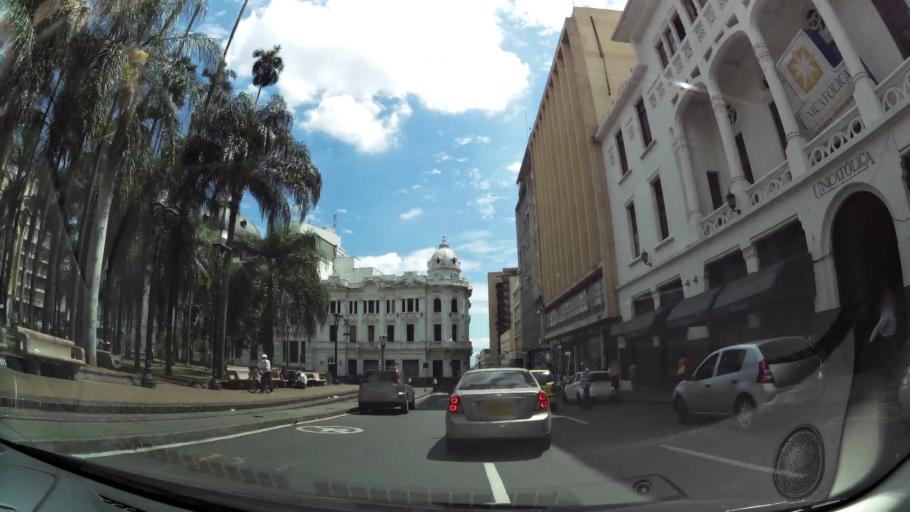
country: CO
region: Valle del Cauca
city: Cali
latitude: 3.4515
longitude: -76.5325
